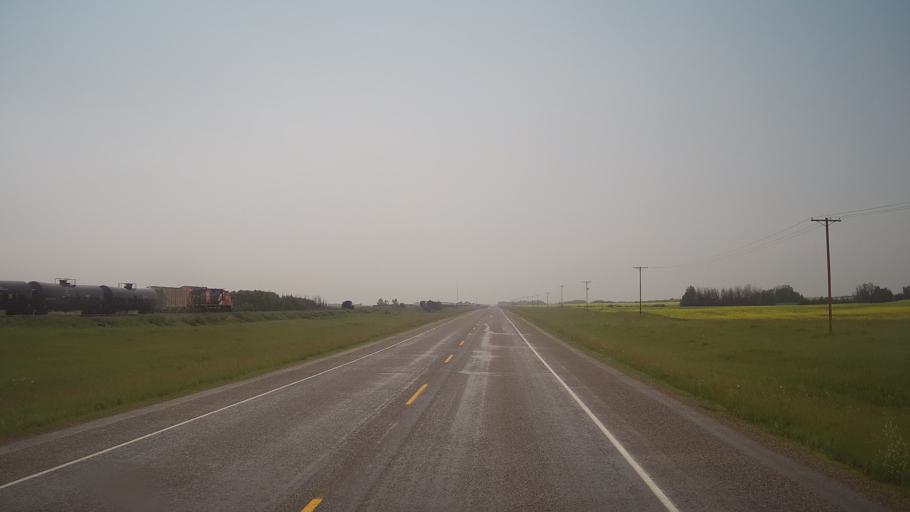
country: CA
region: Saskatchewan
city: Biggar
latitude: 52.1635
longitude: -108.2924
